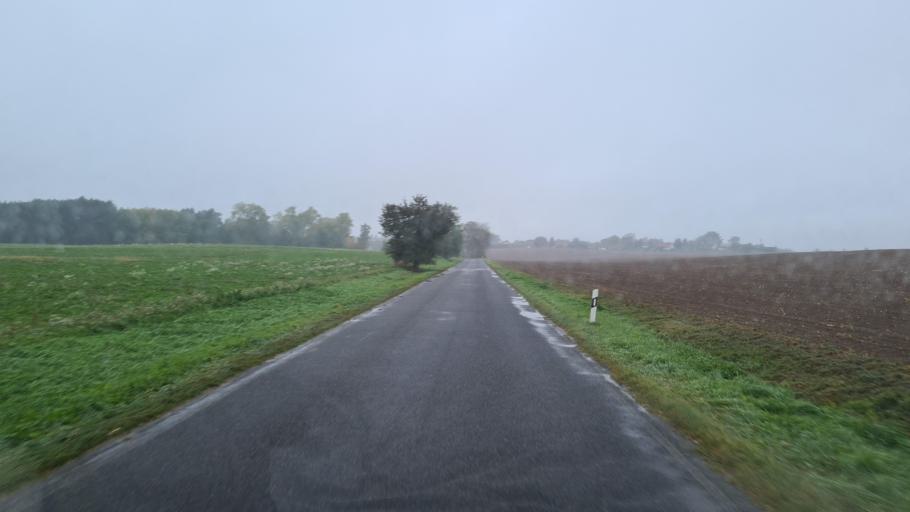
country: DE
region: Brandenburg
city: Furstenwalde
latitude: 52.4308
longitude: 14.0275
